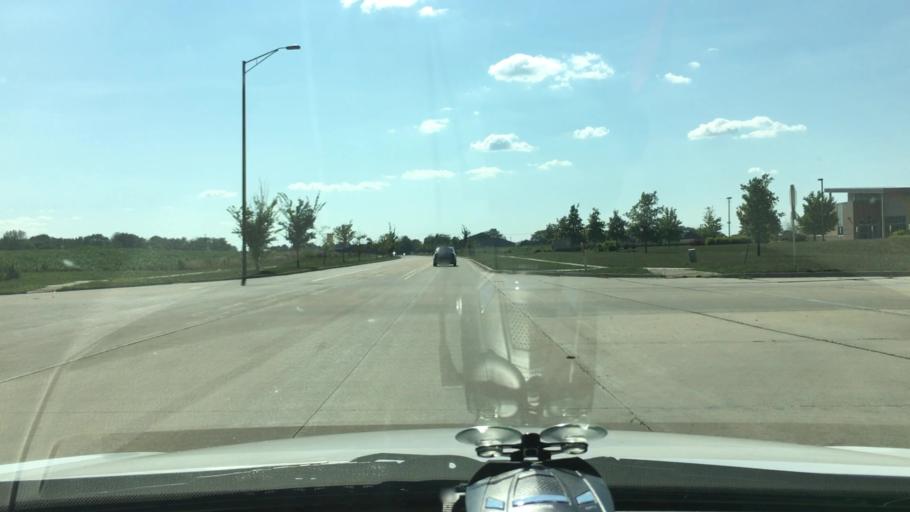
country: US
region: Illinois
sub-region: Champaign County
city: Champaign
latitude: 40.1491
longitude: -88.2618
